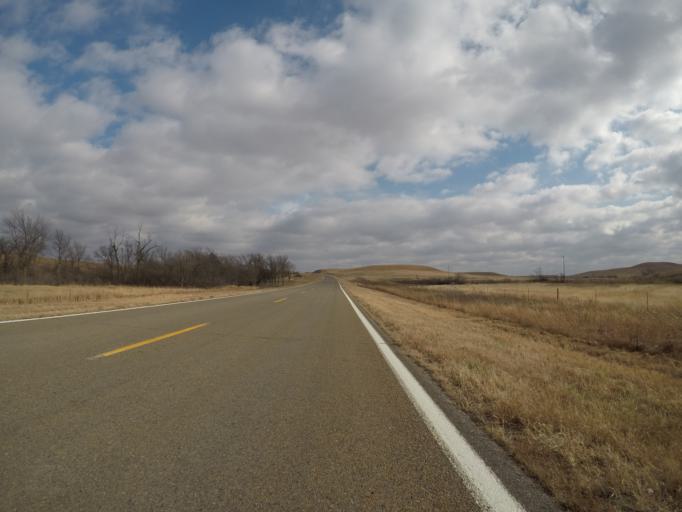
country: US
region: Kansas
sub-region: Wabaunsee County
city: Alma
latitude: 38.8707
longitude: -96.3474
